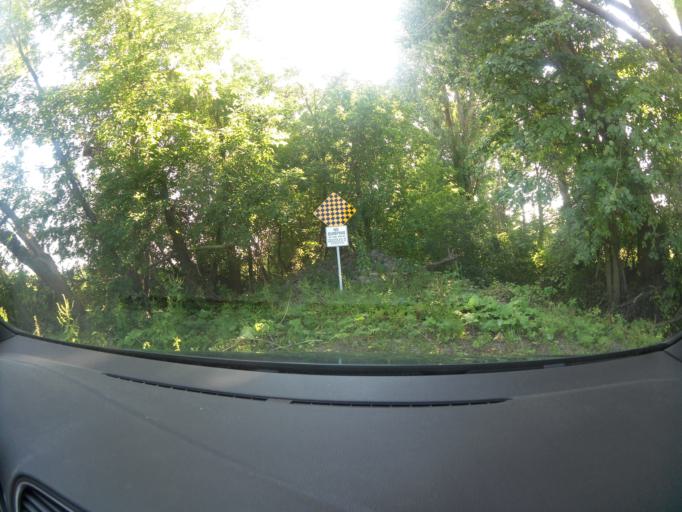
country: CA
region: Ontario
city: Arnprior
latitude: 45.3525
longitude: -76.2816
